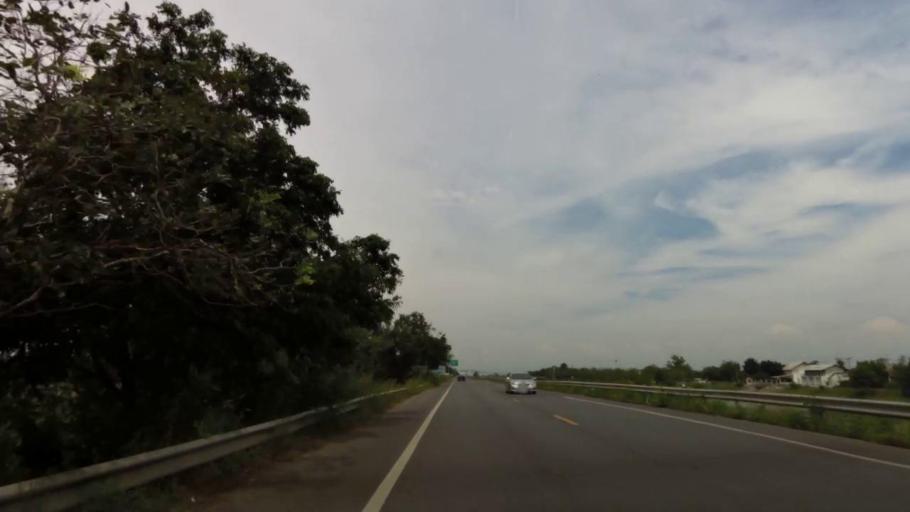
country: TH
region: Lop Buri
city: Ban Mi
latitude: 15.0421
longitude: 100.5649
